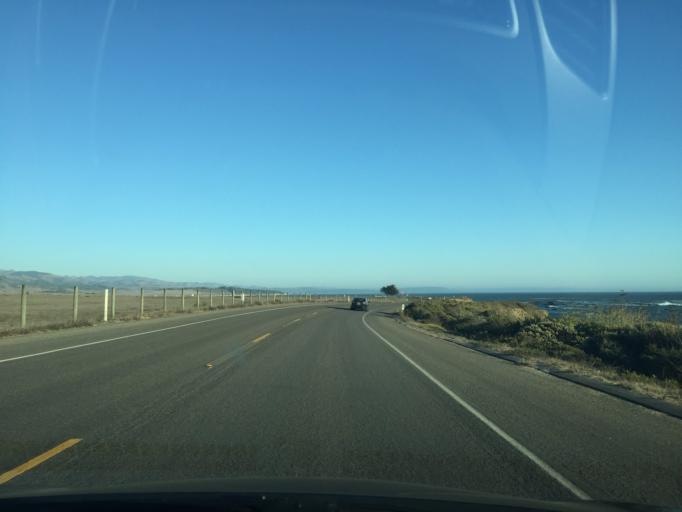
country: US
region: California
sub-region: San Luis Obispo County
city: Cambria
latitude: 35.6561
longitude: -121.2464
